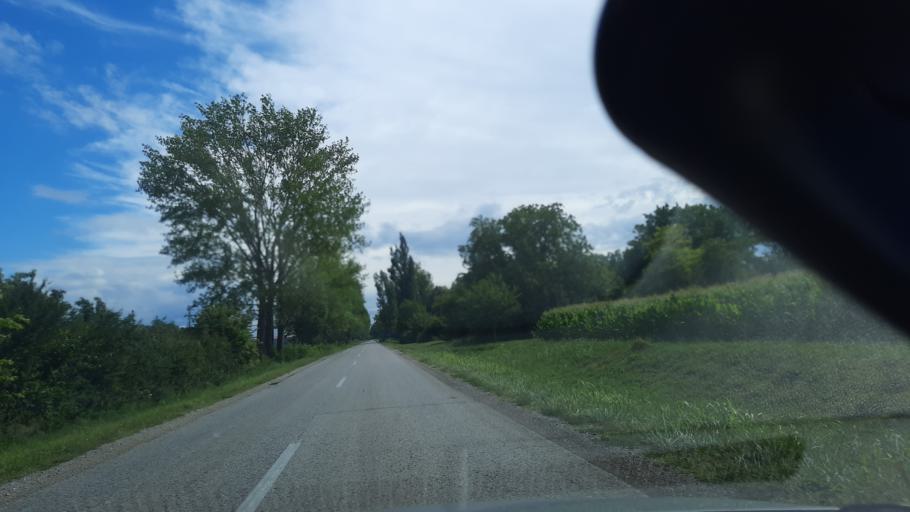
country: RS
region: Autonomna Pokrajina Vojvodina
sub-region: Sremski Okrug
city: Sremska Mitrovica
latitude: 45.0185
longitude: 19.6144
